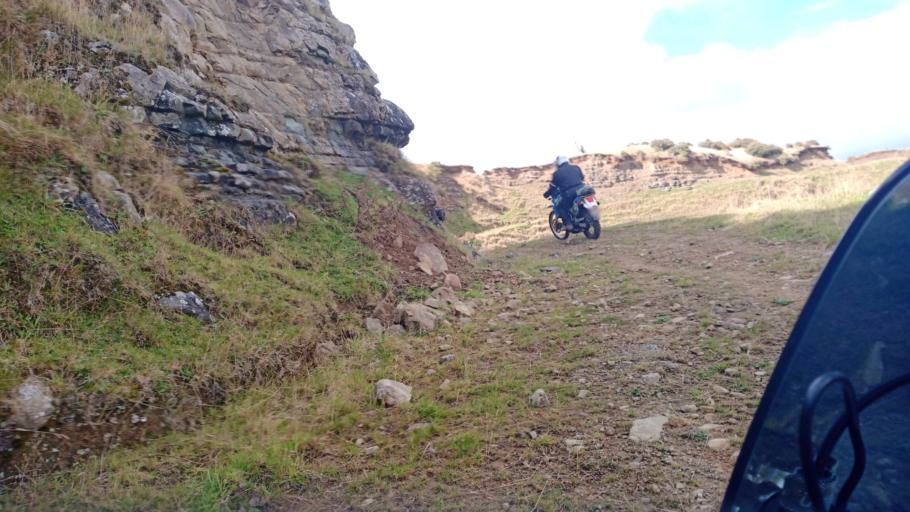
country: NZ
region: Gisborne
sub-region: Gisborne District
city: Gisborne
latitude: -38.4761
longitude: 177.5338
